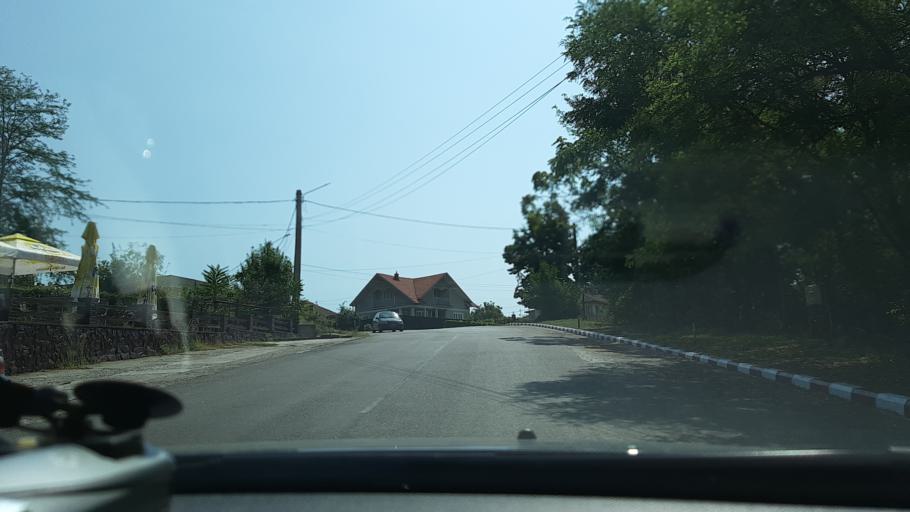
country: RO
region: Gorj
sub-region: Comuna Targu Carbunesti
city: Targu Carbunesti
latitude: 44.9619
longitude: 23.5118
